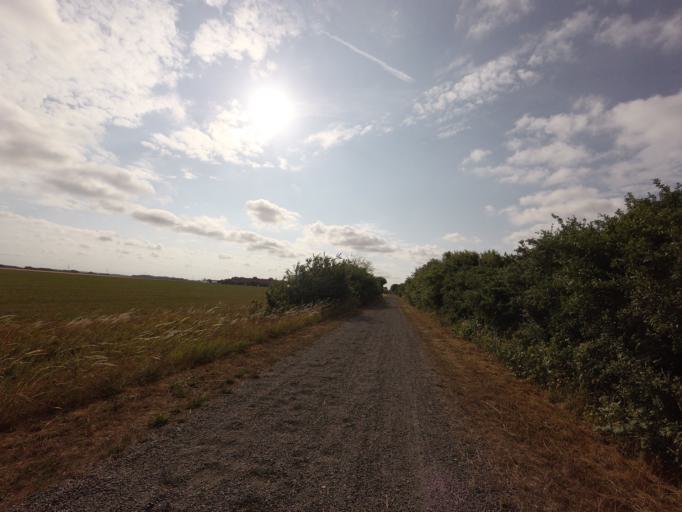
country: SE
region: Skane
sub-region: Helsingborg
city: Odakra
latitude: 56.1579
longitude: 12.7508
